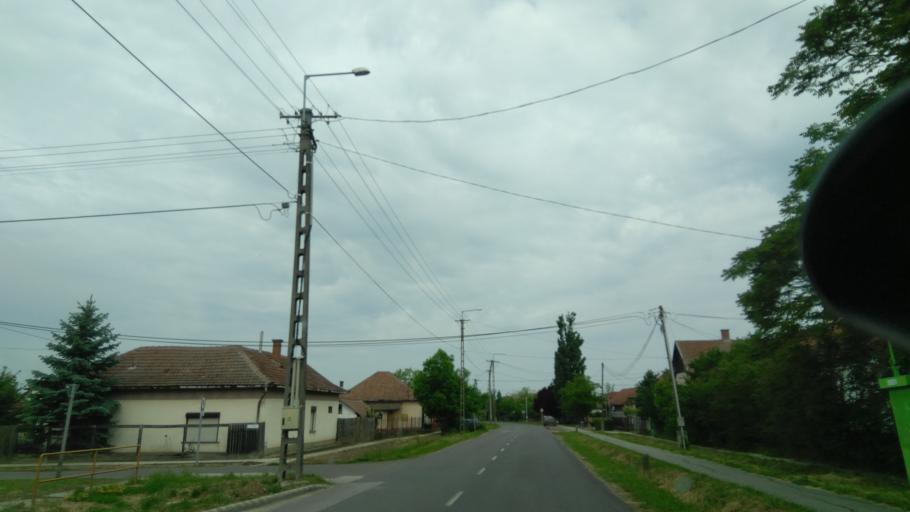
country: HU
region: Bekes
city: Szeghalom
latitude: 47.0350
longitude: 21.1616
